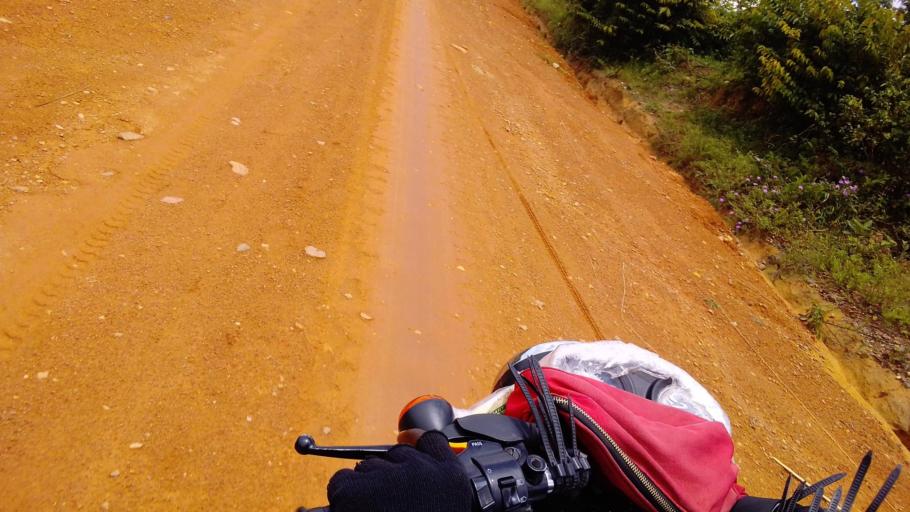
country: SL
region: Eastern Province
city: Koidu
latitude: 8.6926
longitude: -10.9243
